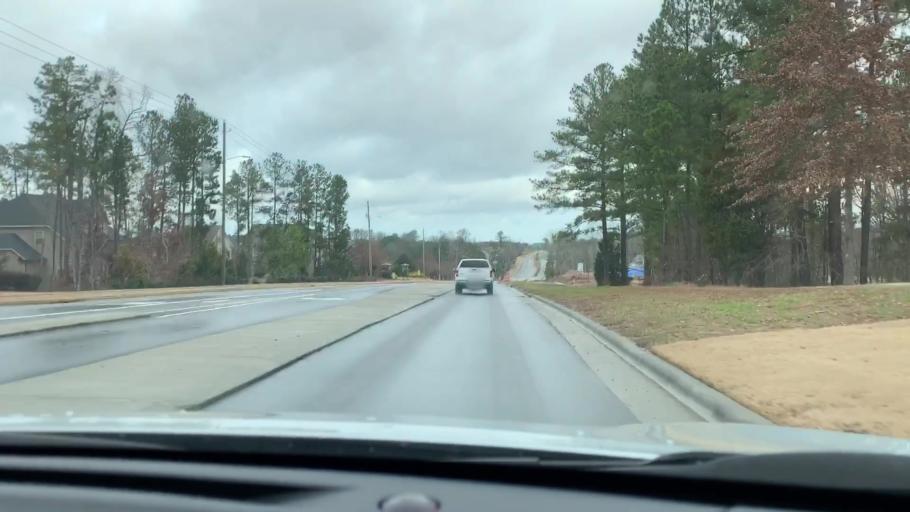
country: US
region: North Carolina
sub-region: Wake County
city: Green Level
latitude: 35.8334
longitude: -78.8992
